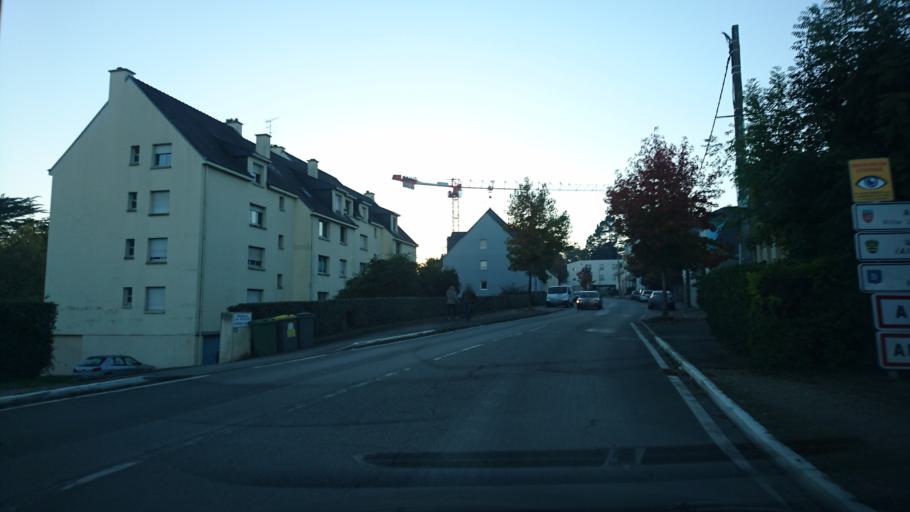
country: FR
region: Brittany
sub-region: Departement du Morbihan
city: Auray
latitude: 47.6687
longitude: -2.9752
